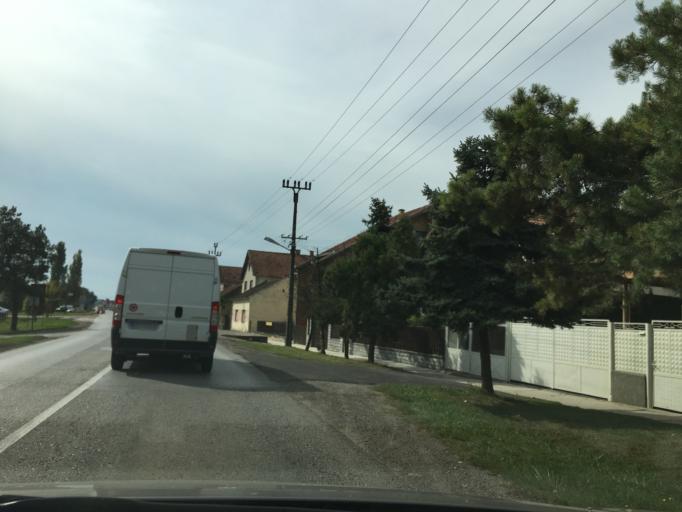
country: RS
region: Autonomna Pokrajina Vojvodina
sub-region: Juznobacki Okrug
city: Temerin
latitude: 45.3681
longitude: 19.8698
